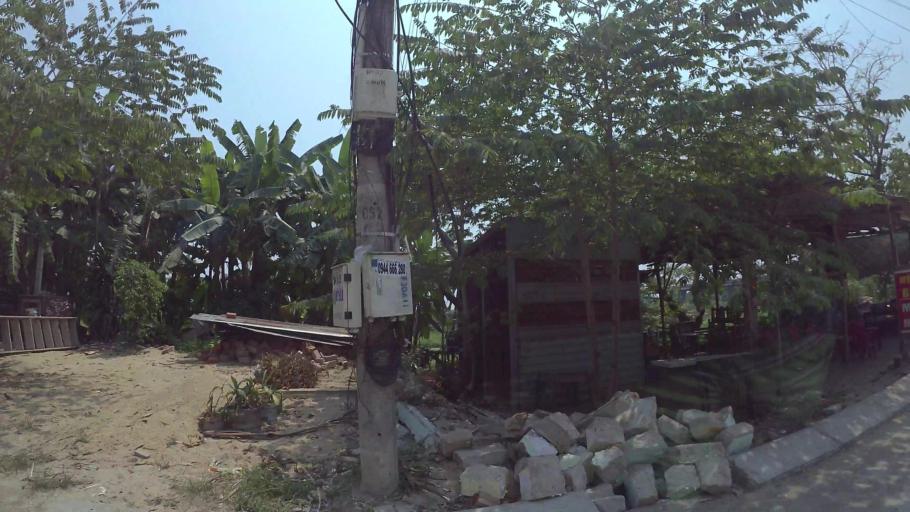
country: VN
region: Da Nang
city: Cam Le
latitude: 16.0192
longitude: 108.2133
